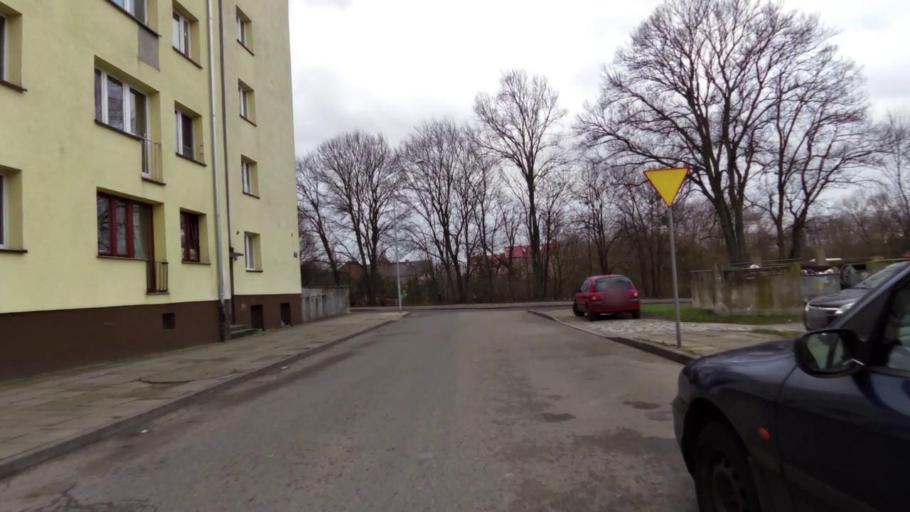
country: PL
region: West Pomeranian Voivodeship
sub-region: Powiat mysliborski
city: Mysliborz
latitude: 52.9243
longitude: 14.8634
